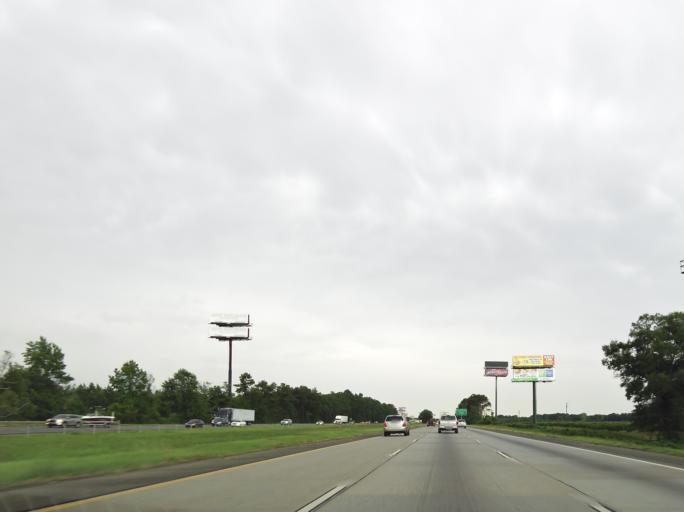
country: US
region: Georgia
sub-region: Peach County
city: Byron
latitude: 32.6034
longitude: -83.7428
